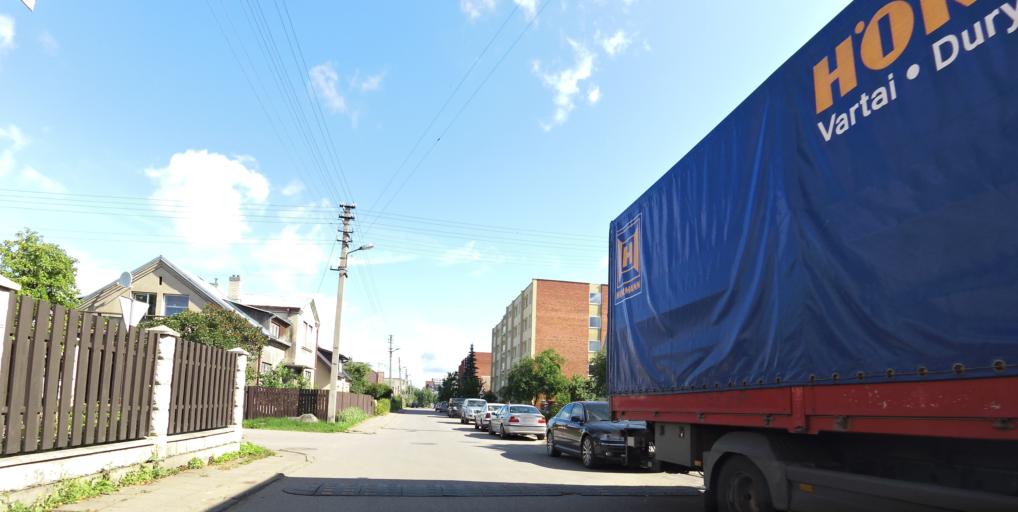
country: LT
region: Vilnius County
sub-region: Vilnius
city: Vilnius
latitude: 54.7080
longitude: 25.2808
